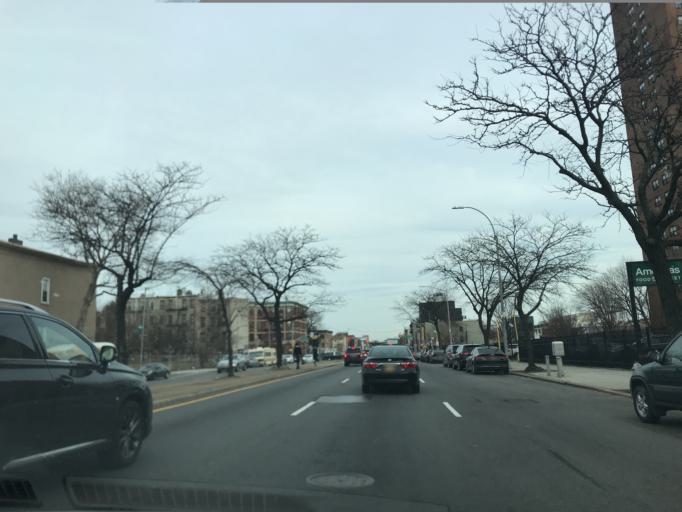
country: US
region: New York
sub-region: Kings County
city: East New York
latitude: 40.6764
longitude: -73.9127
